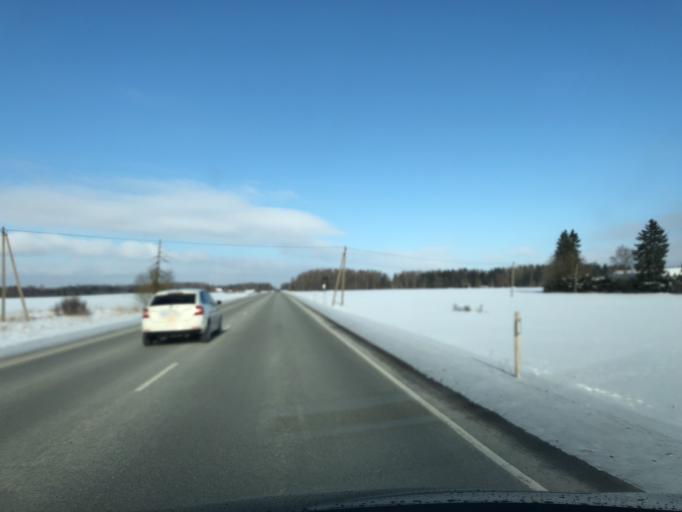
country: EE
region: Jaervamaa
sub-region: Paide linn
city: Paide
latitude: 58.7951
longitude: 25.7581
